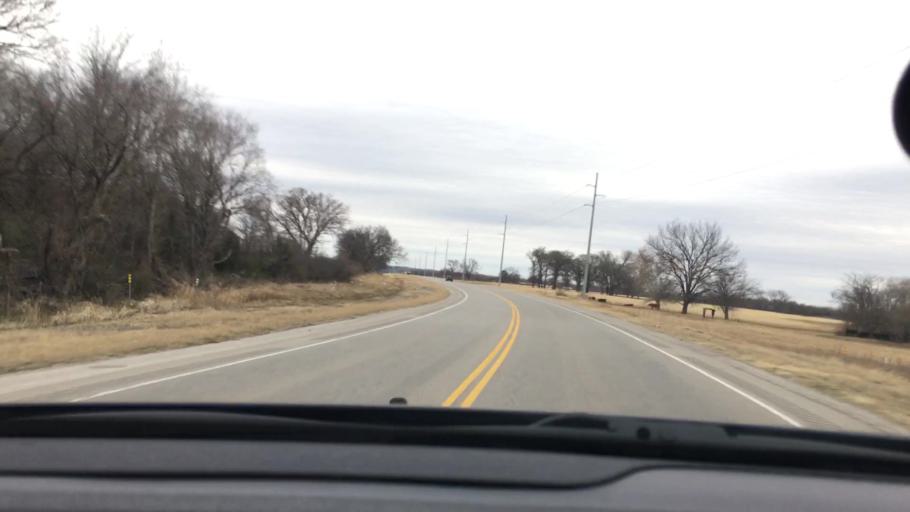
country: US
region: Oklahoma
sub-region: Marshall County
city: Oakland
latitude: 34.1923
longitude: -96.8024
